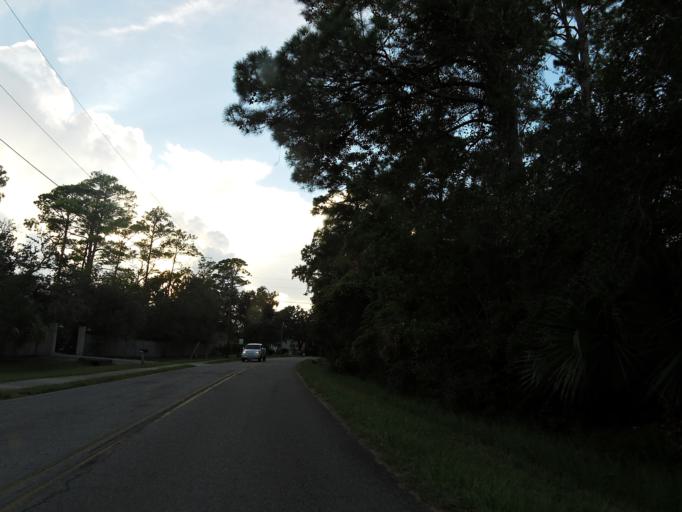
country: US
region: Georgia
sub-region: Camden County
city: St. Marys
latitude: 30.7218
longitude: -81.5564
